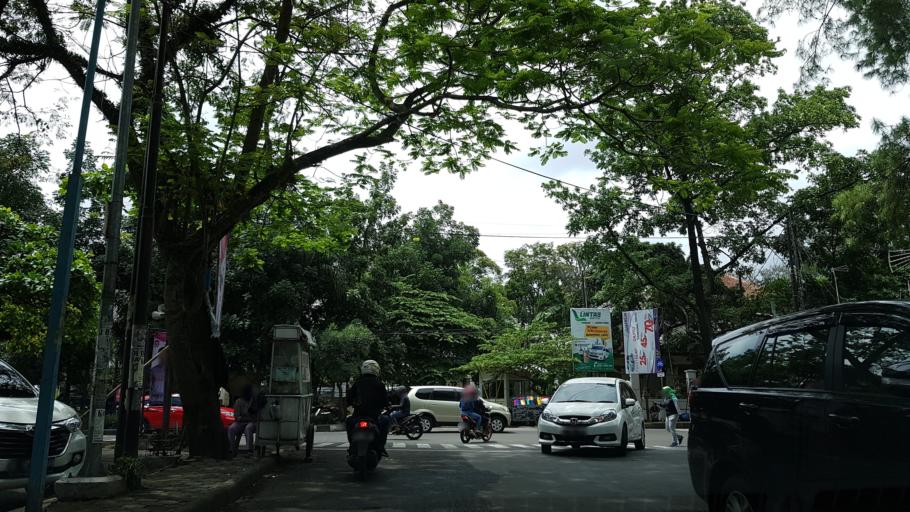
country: ID
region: West Java
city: Bandung
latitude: -6.8958
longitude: 107.6171
